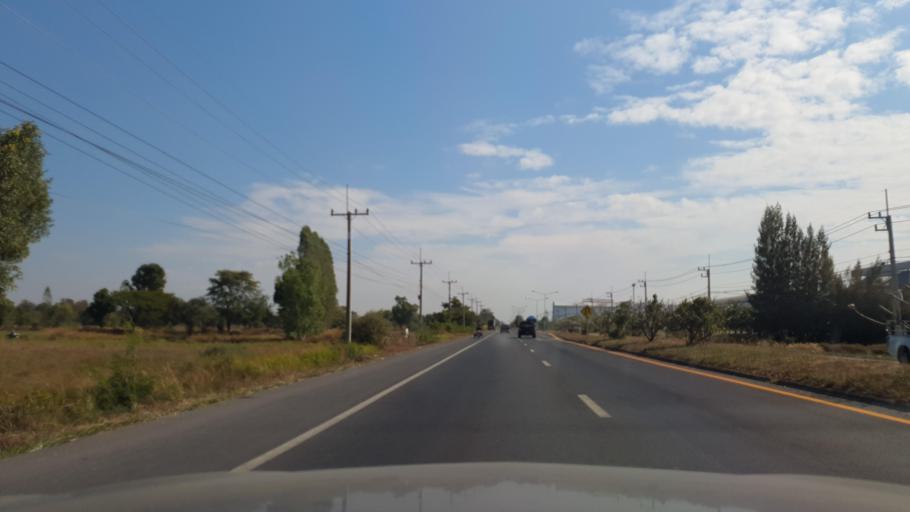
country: TH
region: Maha Sarakham
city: Kantharawichai
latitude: 16.3827
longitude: 103.2156
